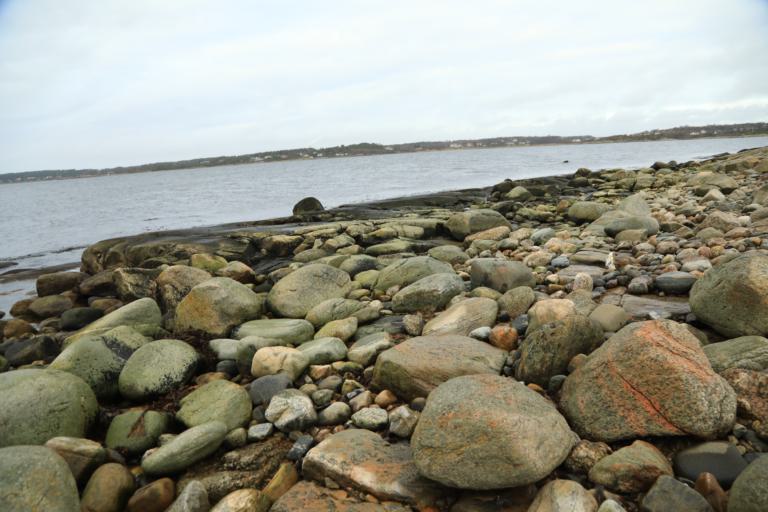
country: SE
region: Halland
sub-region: Varbergs Kommun
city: Varberg
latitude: 57.1790
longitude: 12.2029
